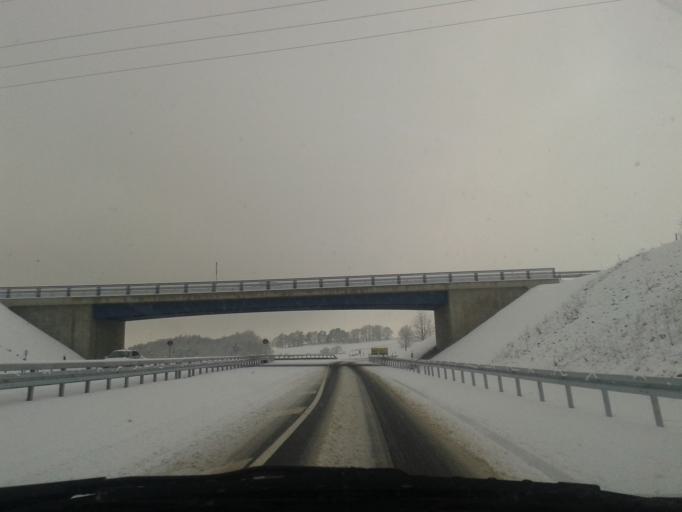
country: DE
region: Saxony
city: Durrrohrsdorf
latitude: 51.0110
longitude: 13.9553
